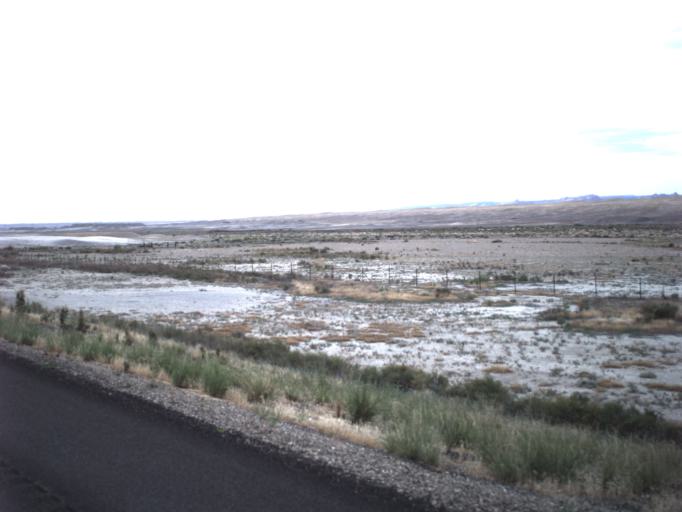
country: US
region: Utah
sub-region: Carbon County
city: East Carbon City
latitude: 39.0640
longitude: -110.3137
